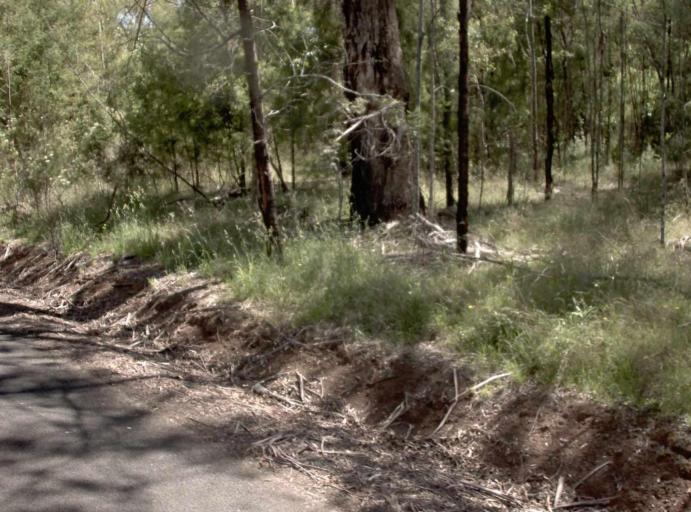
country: AU
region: Victoria
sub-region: East Gippsland
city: Lakes Entrance
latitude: -37.4396
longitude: 148.1913
